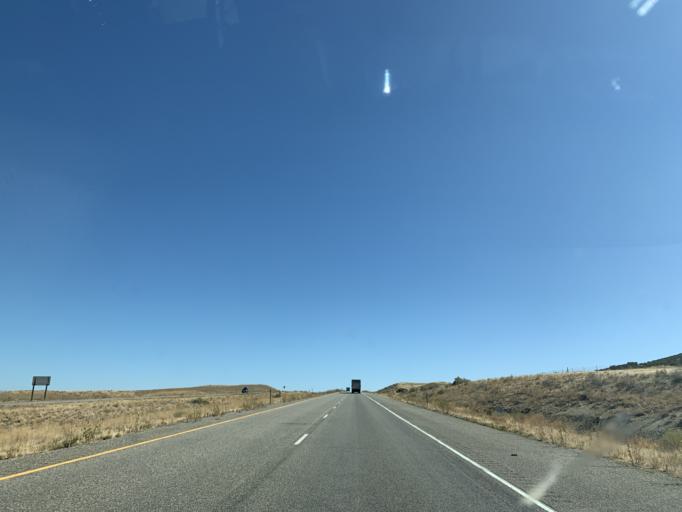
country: US
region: Colorado
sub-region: Mesa County
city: Loma
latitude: 39.2198
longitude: -108.8828
